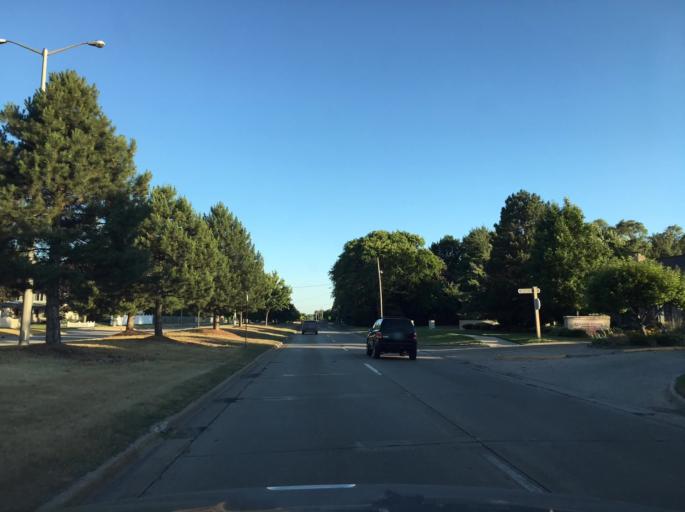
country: US
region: Michigan
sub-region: Macomb County
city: Utica
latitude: 42.6076
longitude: -82.9922
